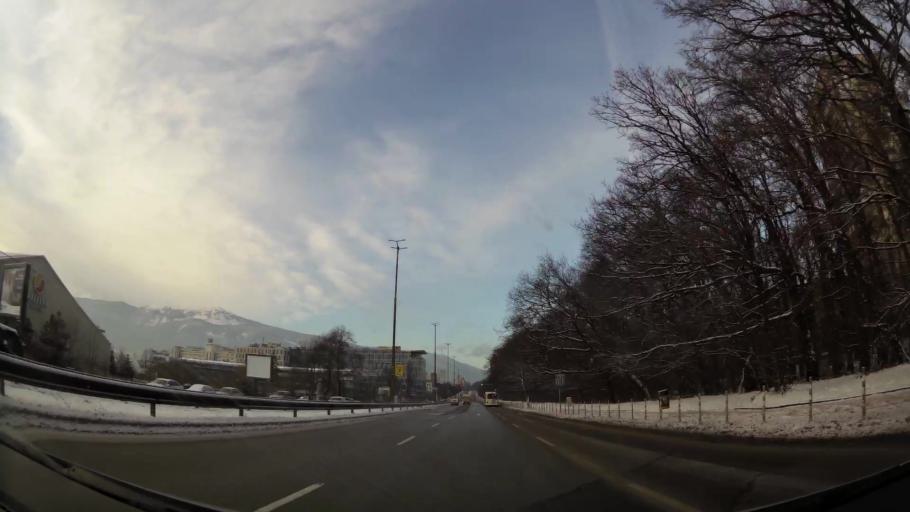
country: BG
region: Sofia-Capital
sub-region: Stolichna Obshtina
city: Sofia
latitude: 42.6682
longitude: 23.3283
